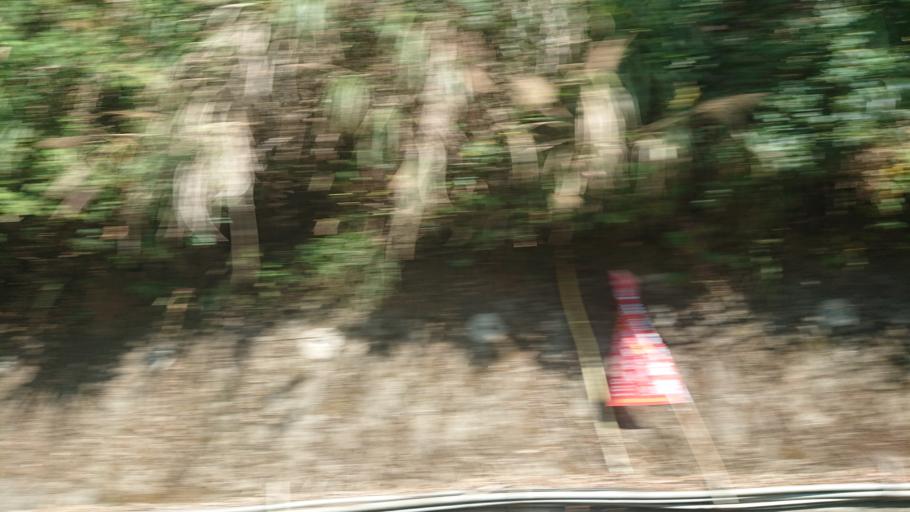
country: TW
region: Taiwan
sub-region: Chiayi
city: Jiayi Shi
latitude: 23.4713
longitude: 120.7067
